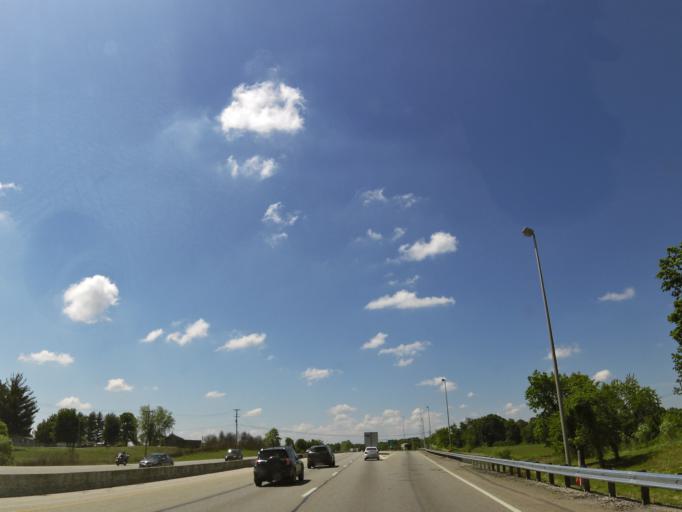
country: US
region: Kentucky
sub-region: Laurel County
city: London
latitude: 37.0524
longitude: -84.0987
